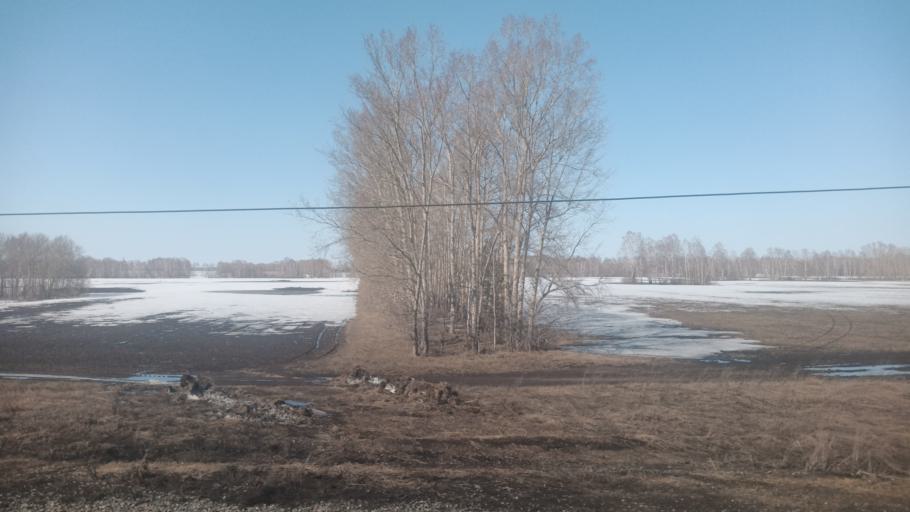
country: RU
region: Altai Krai
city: Logovskoye
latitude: 53.4867
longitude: 84.1592
